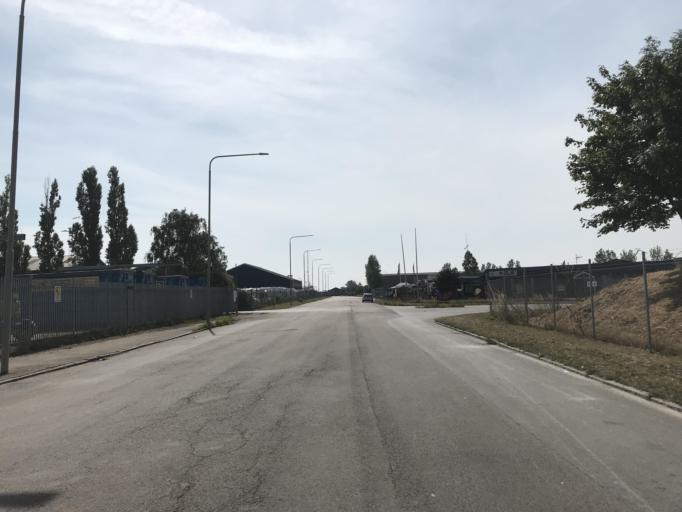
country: SE
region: Skane
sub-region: Landskrona
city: Landskrona
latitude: 55.8639
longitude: 12.8505
